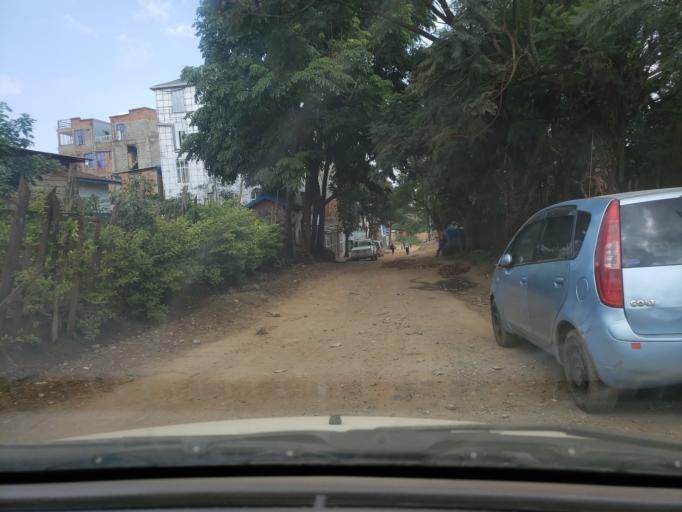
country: RW
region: Western Province
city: Cyangugu
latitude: -2.4955
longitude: 28.8882
